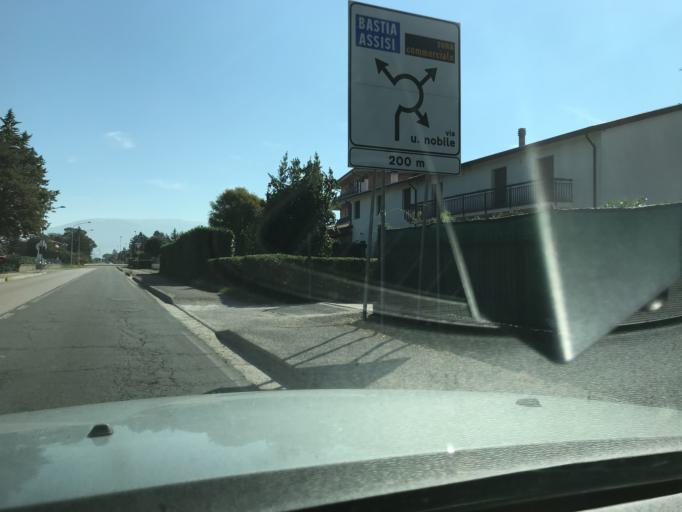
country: IT
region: Umbria
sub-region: Provincia di Perugia
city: Ospedalicchio
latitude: 43.0790
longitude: 12.5064
